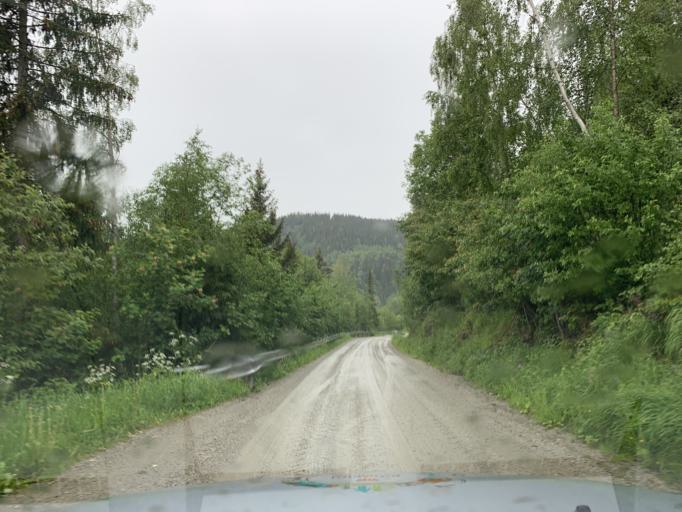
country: NO
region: Oppland
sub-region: Oyer
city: Tretten
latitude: 61.3883
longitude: 10.2801
